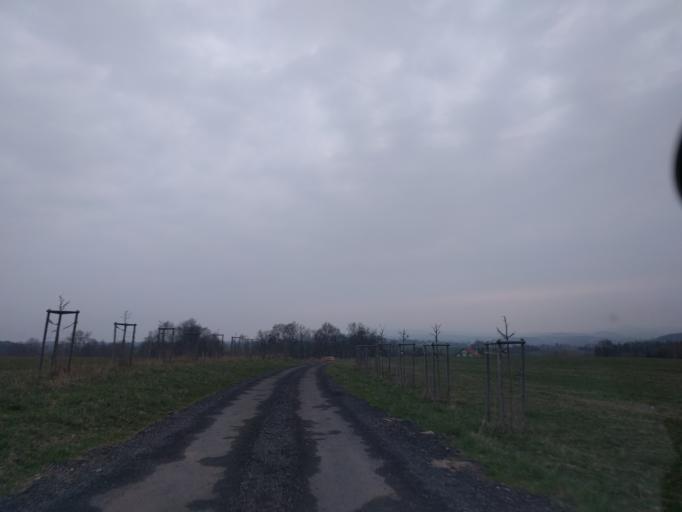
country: CZ
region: Karlovarsky
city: Bochov
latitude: 50.1130
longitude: 13.0914
